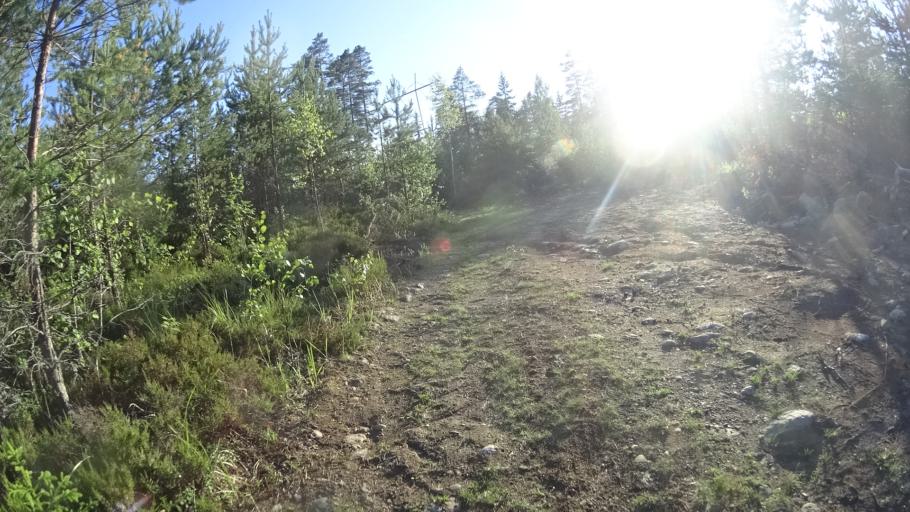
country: FI
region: Uusimaa
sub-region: Helsinki
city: Karkkila
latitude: 60.5950
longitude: 24.1055
